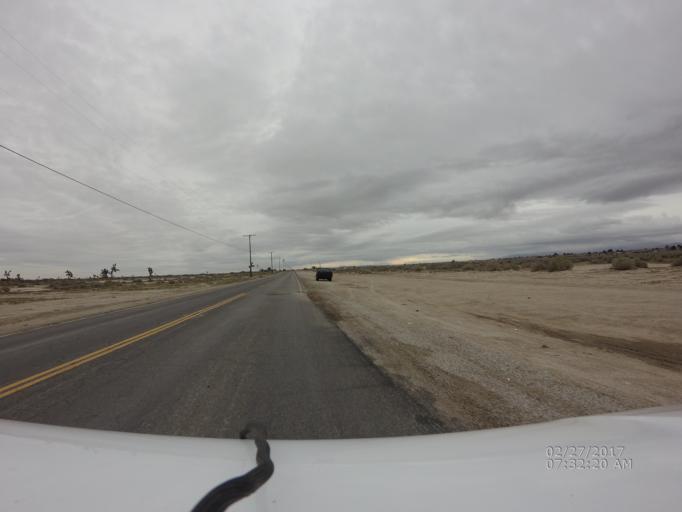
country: US
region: California
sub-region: Los Angeles County
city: Lancaster
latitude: 34.7185
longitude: -118.1297
